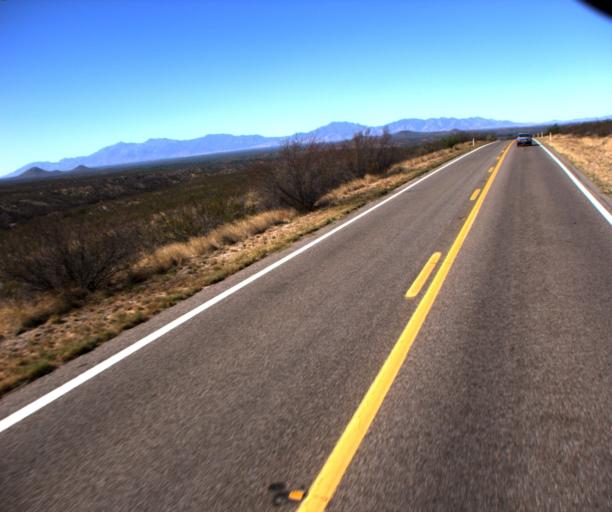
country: US
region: Arizona
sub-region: Cochise County
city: Tombstone
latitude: 31.7367
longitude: -110.1658
